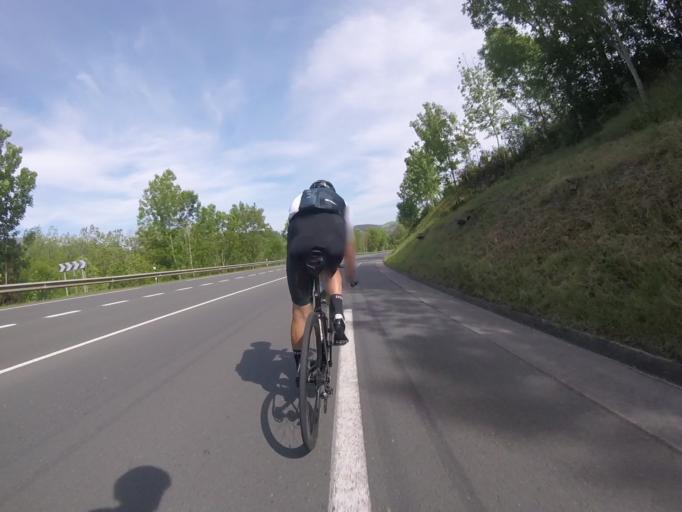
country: ES
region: Basque Country
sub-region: Provincia de Guipuzcoa
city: Cestona
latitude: 43.2594
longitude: -2.2713
